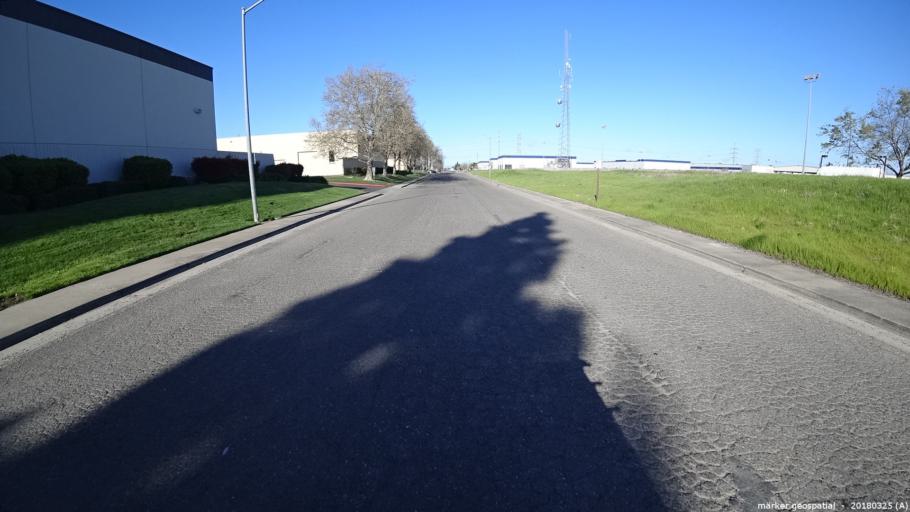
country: US
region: California
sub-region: Sacramento County
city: Rio Linda
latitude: 38.6511
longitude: -121.4814
